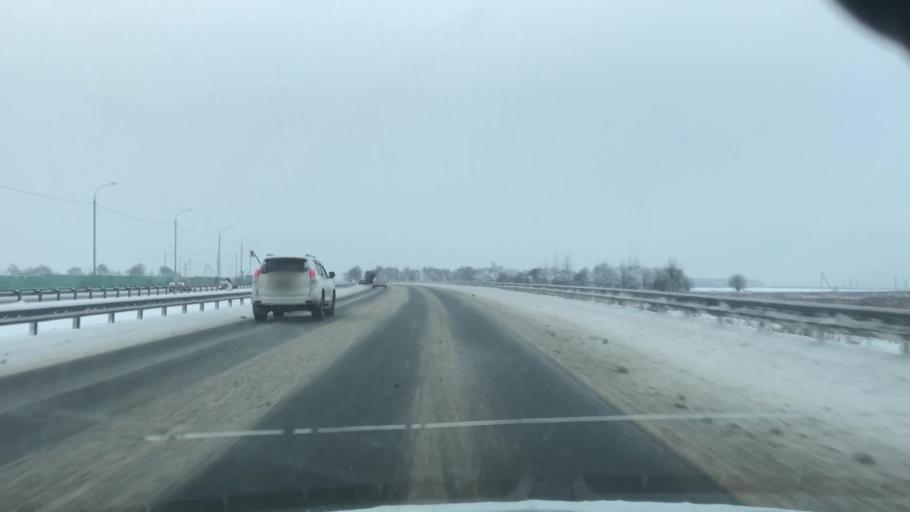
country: RU
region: Moskovskaya
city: Mikhnevo
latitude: 55.1170
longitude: 37.9271
